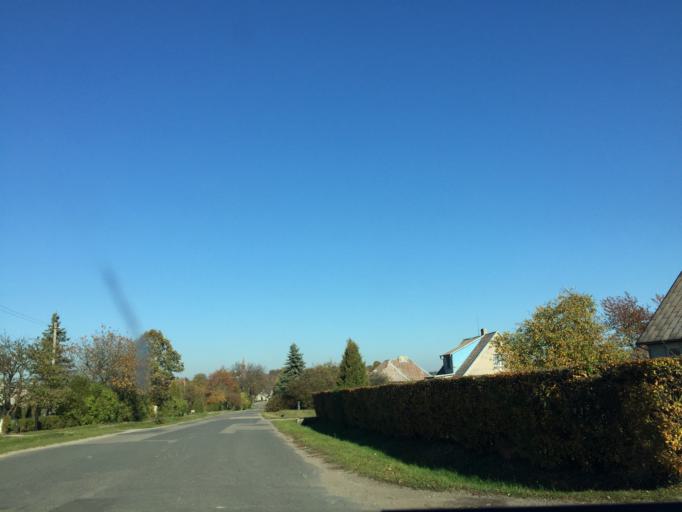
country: LT
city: Salantai
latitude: 55.9919
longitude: 21.6708
